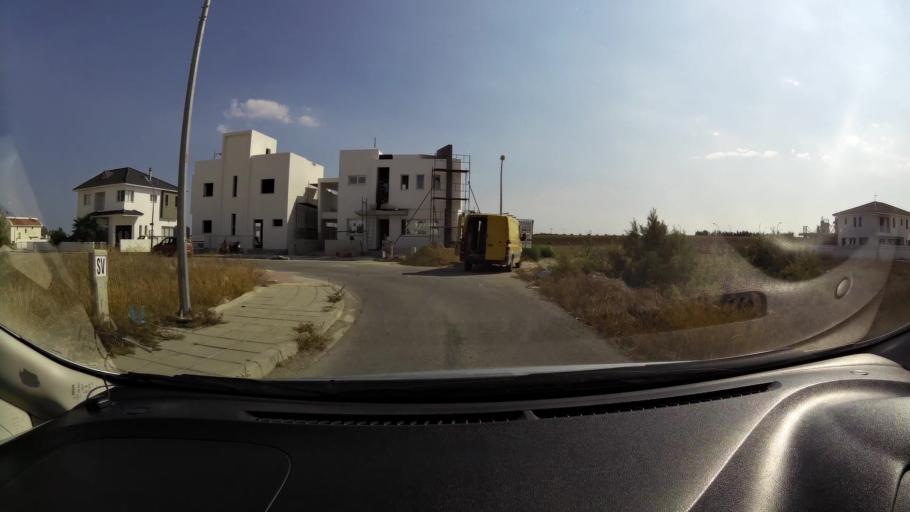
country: CY
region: Larnaka
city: Dhromolaxia
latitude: 34.9033
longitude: 33.5824
